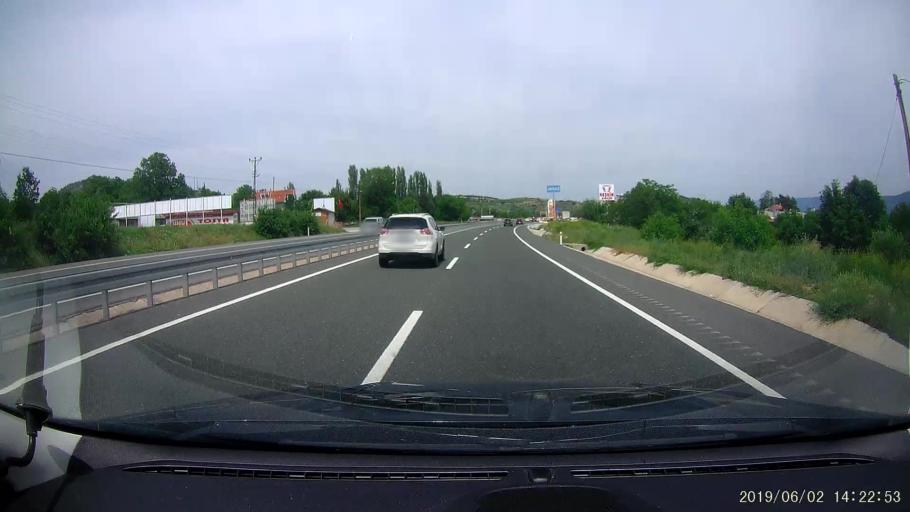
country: TR
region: Kastamonu
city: Tosya
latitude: 40.9996
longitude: 34.0250
